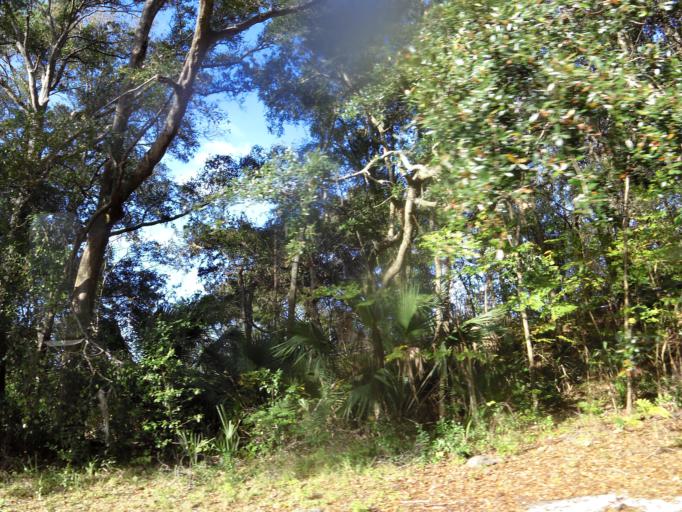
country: US
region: Florida
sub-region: Duval County
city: Jacksonville
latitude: 30.2949
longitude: -81.6156
